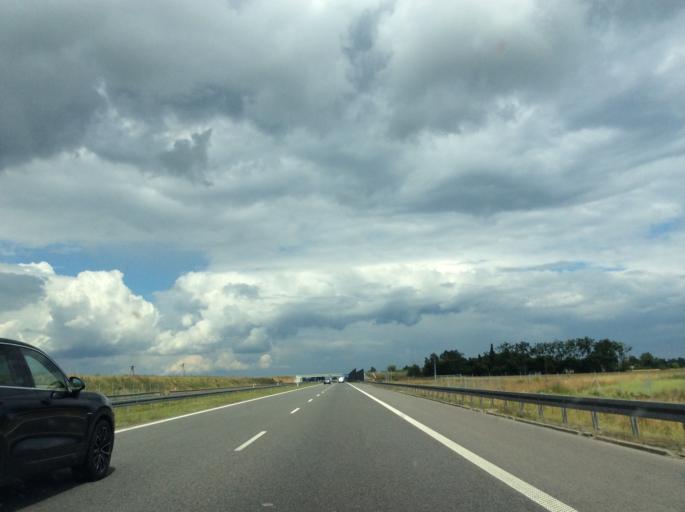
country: PL
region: Masovian Voivodeship
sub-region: Powiat warszawski zachodni
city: Bieniewice
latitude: 52.1344
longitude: 20.5622
